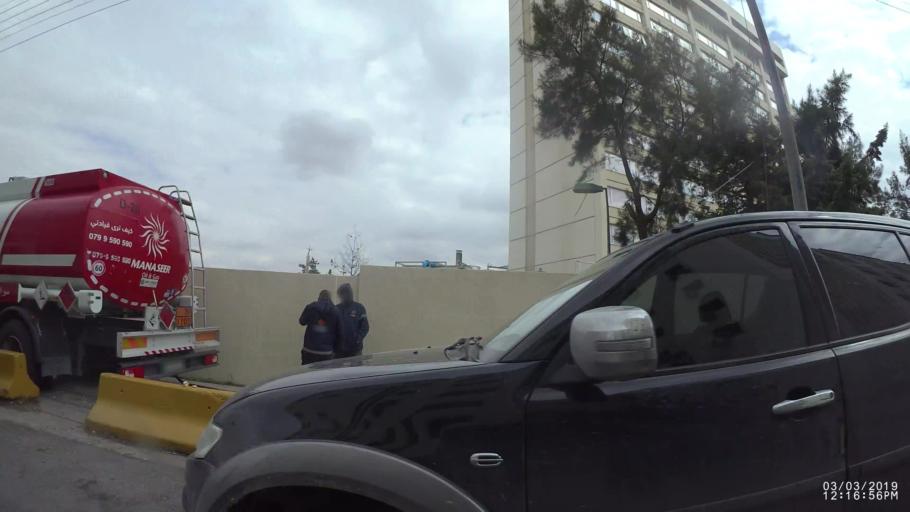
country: JO
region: Amman
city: Amman
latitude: 31.9740
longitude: 35.9059
